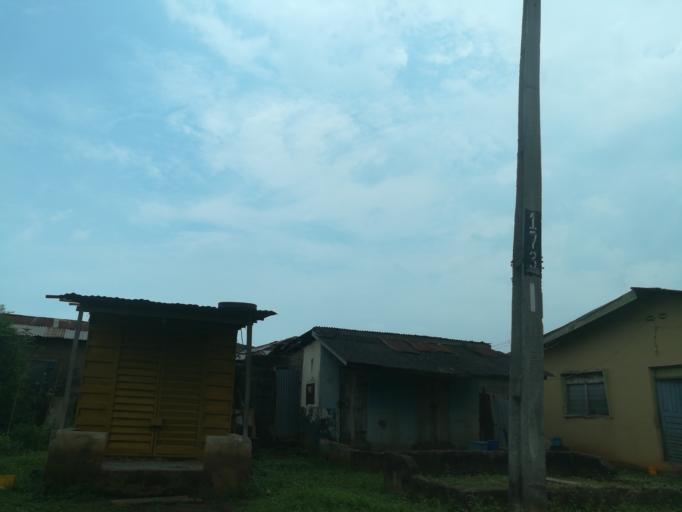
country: NG
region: Lagos
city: Ikorodu
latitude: 6.5659
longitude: 3.5948
